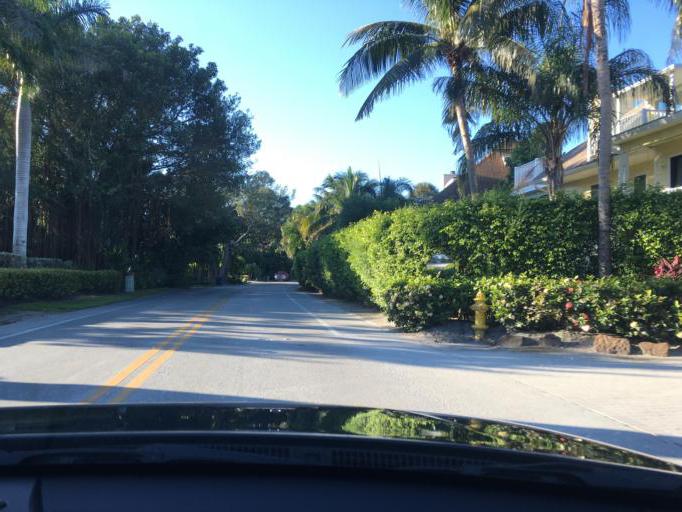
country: US
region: Florida
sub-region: Lee County
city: Saint James City
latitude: 26.5208
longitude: -82.1898
